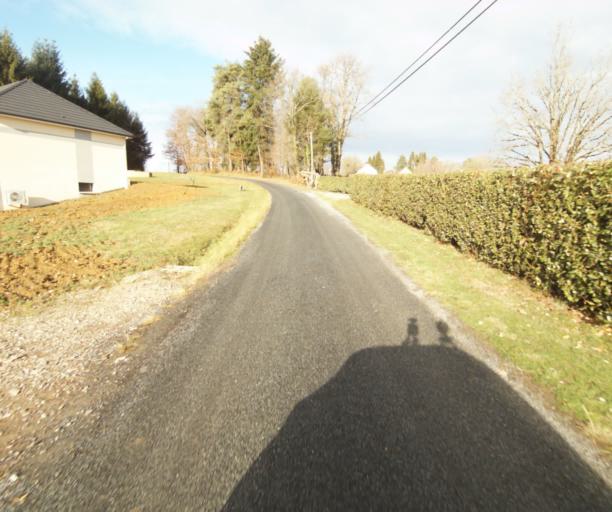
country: FR
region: Limousin
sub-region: Departement de la Correze
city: Saint-Mexant
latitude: 45.2751
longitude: 1.6093
